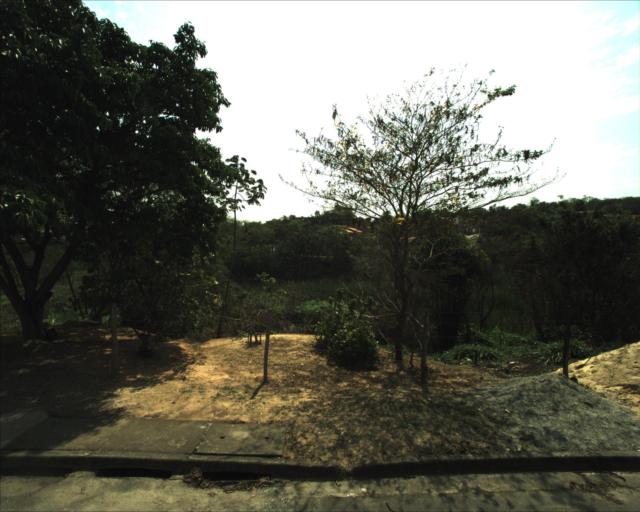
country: BR
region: Sao Paulo
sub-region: Sorocaba
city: Sorocaba
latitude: -23.4414
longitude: -47.4825
